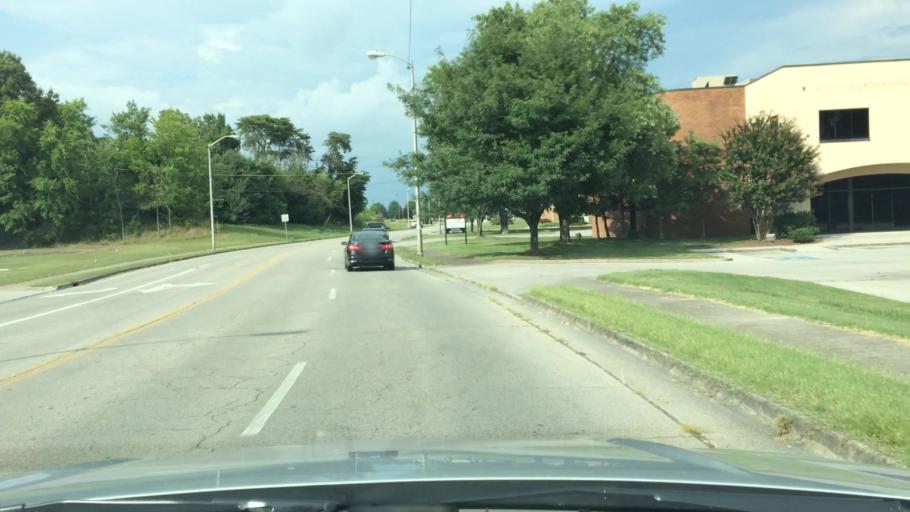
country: US
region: Tennessee
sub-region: Blount County
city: Maryville
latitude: 35.7651
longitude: -83.9794
